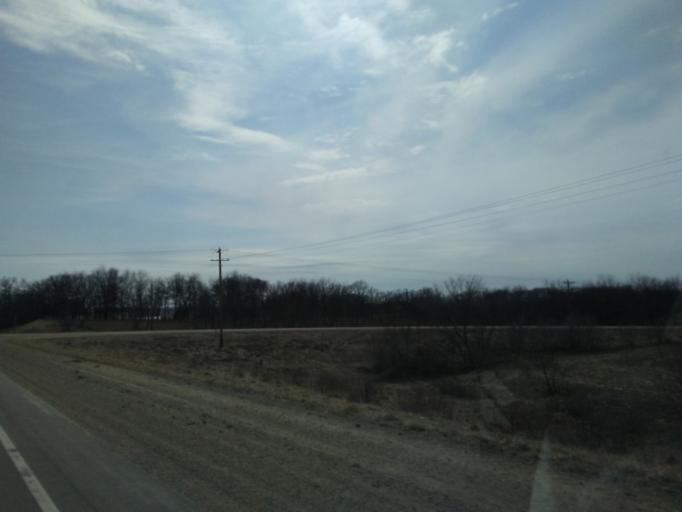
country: US
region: Iowa
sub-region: Winneshiek County
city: Decorah
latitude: 43.4295
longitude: -91.8597
